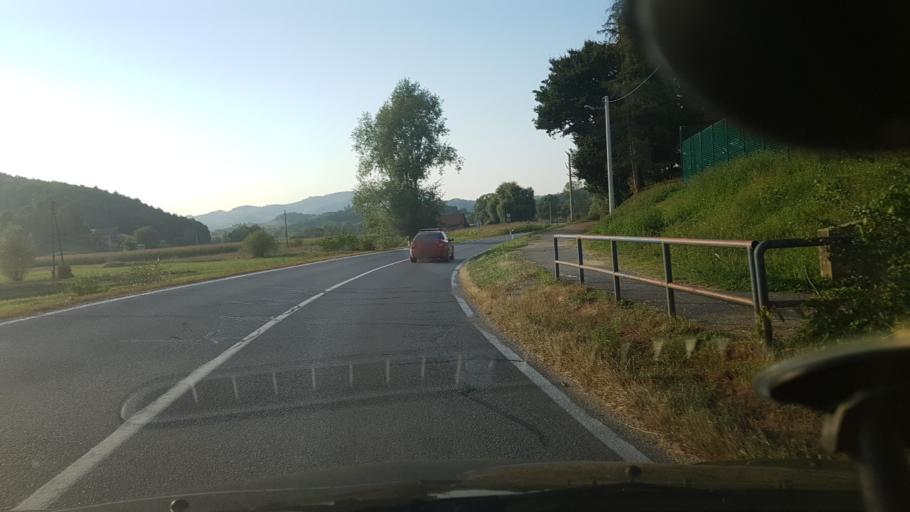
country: HR
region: Krapinsko-Zagorska
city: Pregrada
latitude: 46.1364
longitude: 15.7932
